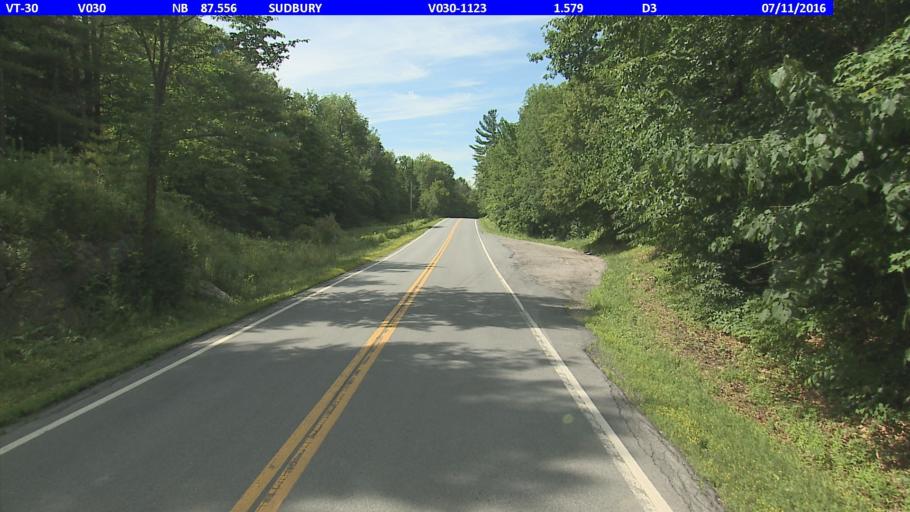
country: US
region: Vermont
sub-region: Rutland County
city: Brandon
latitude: 43.7714
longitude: -73.2001
